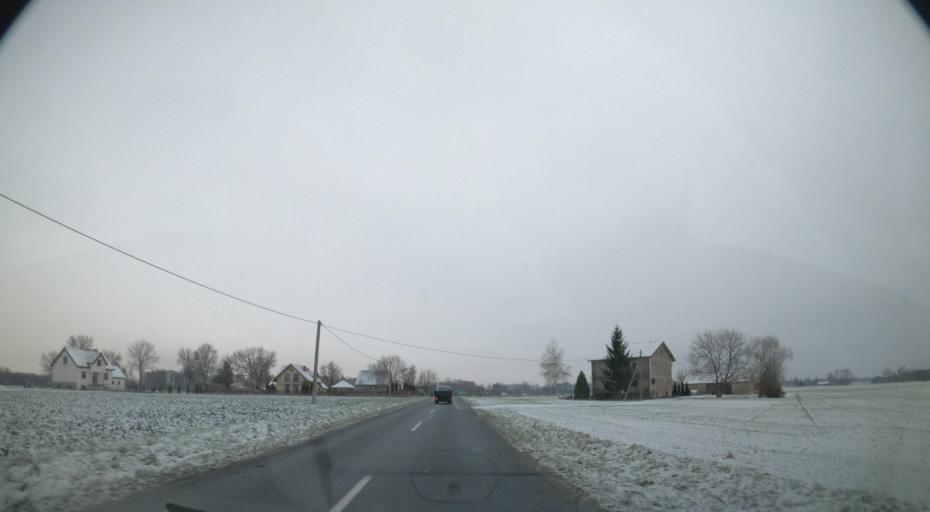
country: PL
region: Kujawsko-Pomorskie
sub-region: Powiat lipnowski
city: Dobrzyn nad Wisla
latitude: 52.6547
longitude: 19.3953
